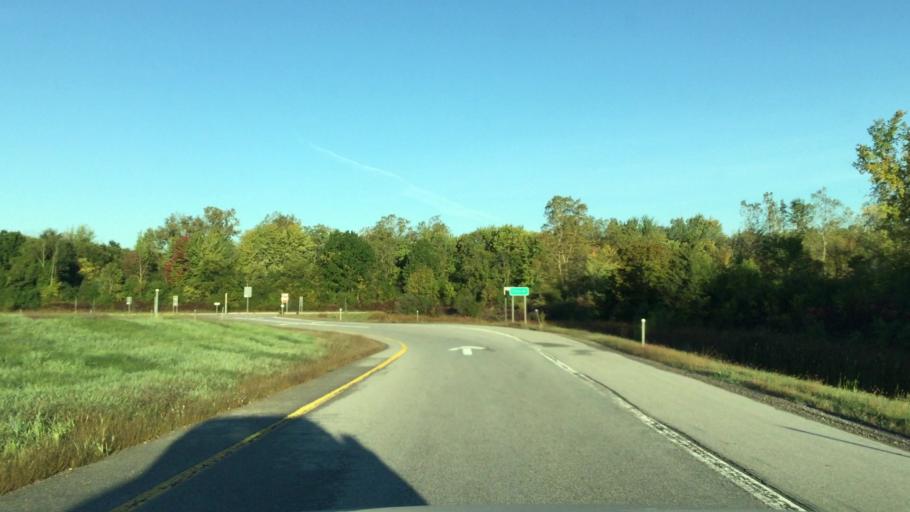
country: US
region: Michigan
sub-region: Genesee County
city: Beecher
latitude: 43.0982
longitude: -83.7319
